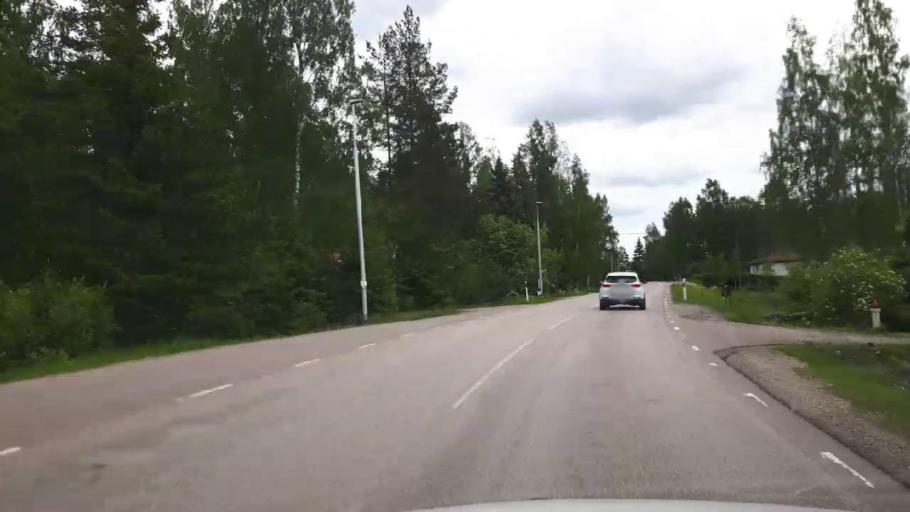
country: SE
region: Vaestmanland
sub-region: Norbergs Kommun
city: Norberg
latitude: 60.1058
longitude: 15.9241
